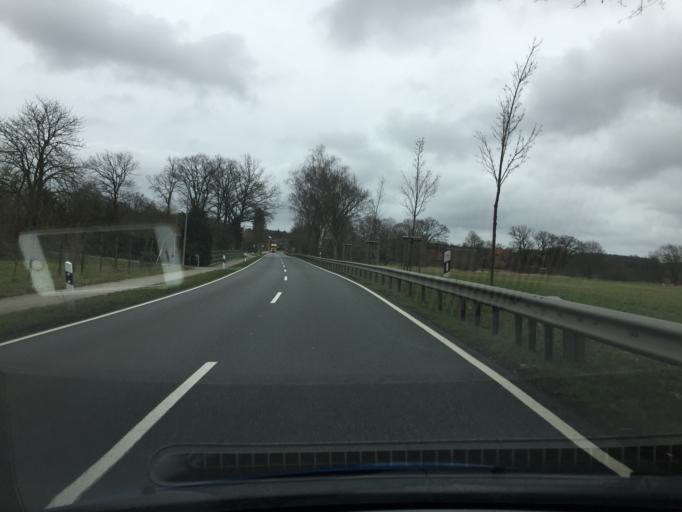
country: DE
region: Lower Saxony
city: Rosche
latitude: 53.0239
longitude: 10.7503
